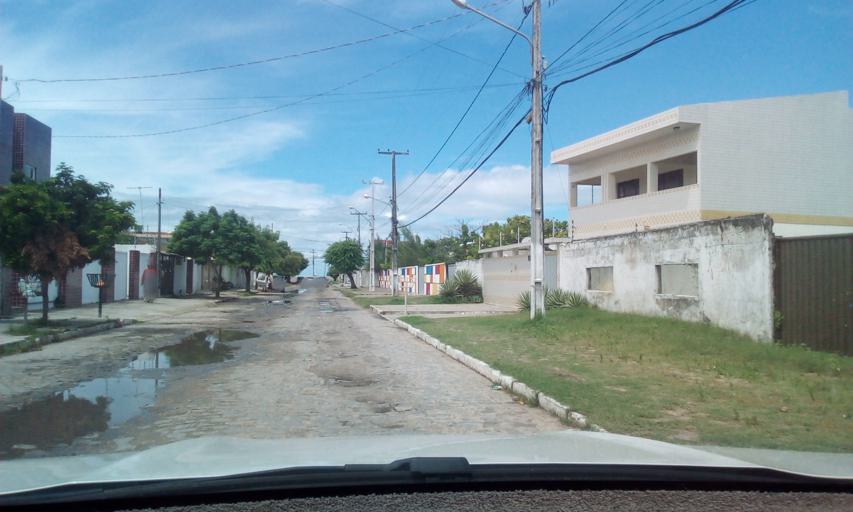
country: BR
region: Paraiba
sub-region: Cabedelo
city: Cabedelo
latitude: -6.9869
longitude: -34.8305
